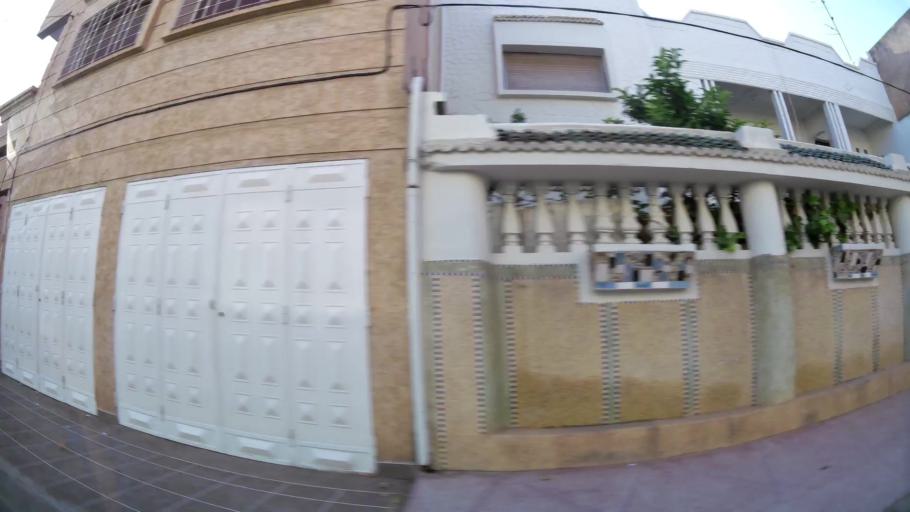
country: MA
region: Oriental
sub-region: Oujda-Angad
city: Oujda
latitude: 34.6716
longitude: -1.9264
